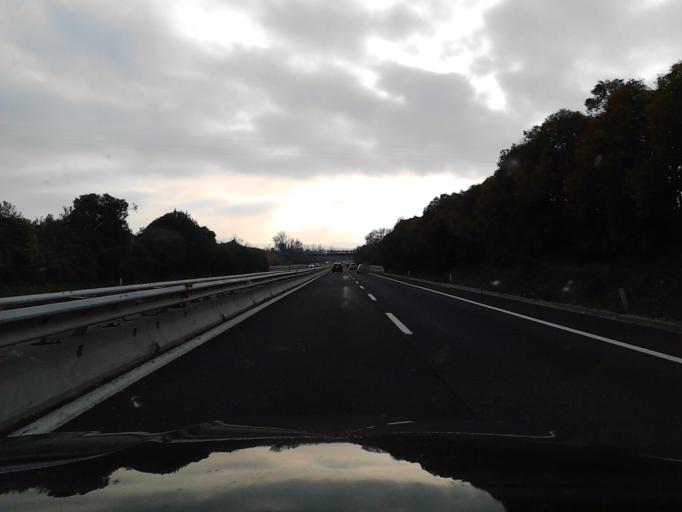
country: IT
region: Abruzzo
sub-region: Provincia di Teramo
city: Colleranesco
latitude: 42.7331
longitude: 13.9295
